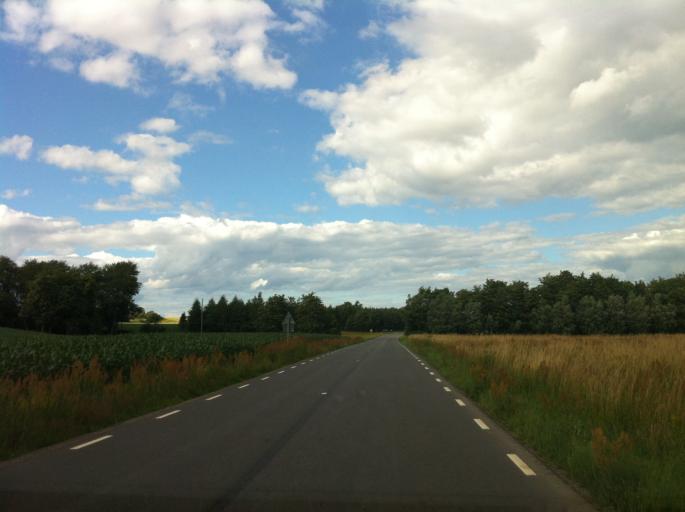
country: SE
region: Skane
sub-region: Simrishamns Kommun
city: Simrishamn
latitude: 55.4280
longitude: 14.2199
